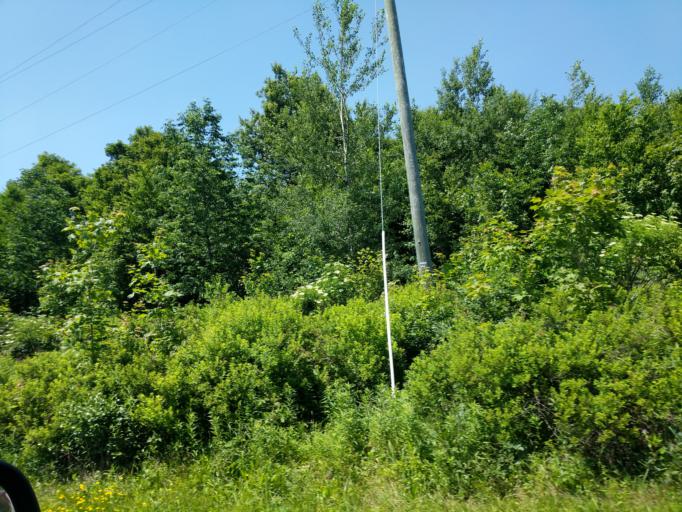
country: US
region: New York
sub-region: Sullivan County
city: Livingston Manor
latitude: 41.8947
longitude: -74.9553
